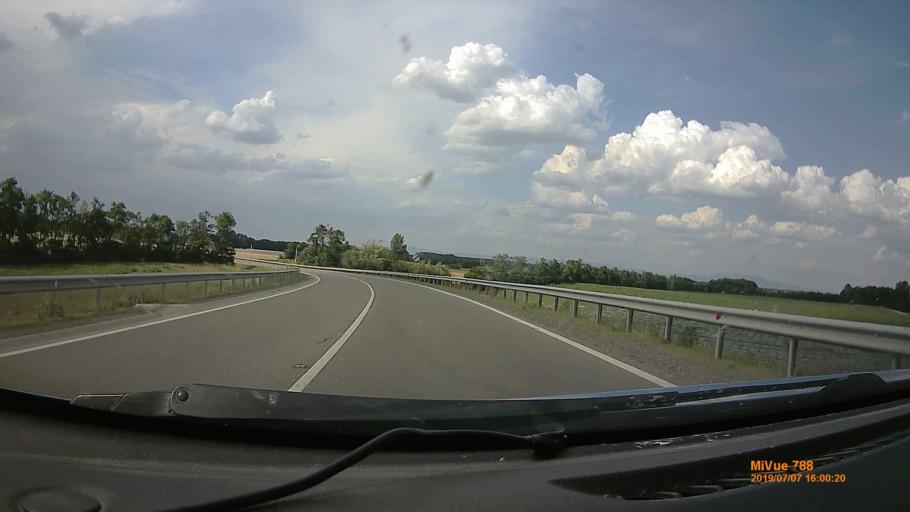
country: HU
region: Heves
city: Boldog
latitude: 47.5980
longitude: 19.7497
